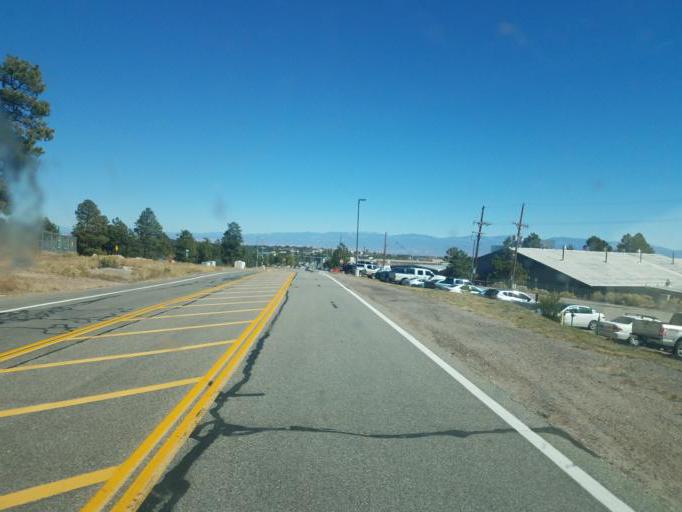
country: US
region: New Mexico
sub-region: Los Alamos County
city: Los Alamos
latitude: 35.8755
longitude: -106.3308
